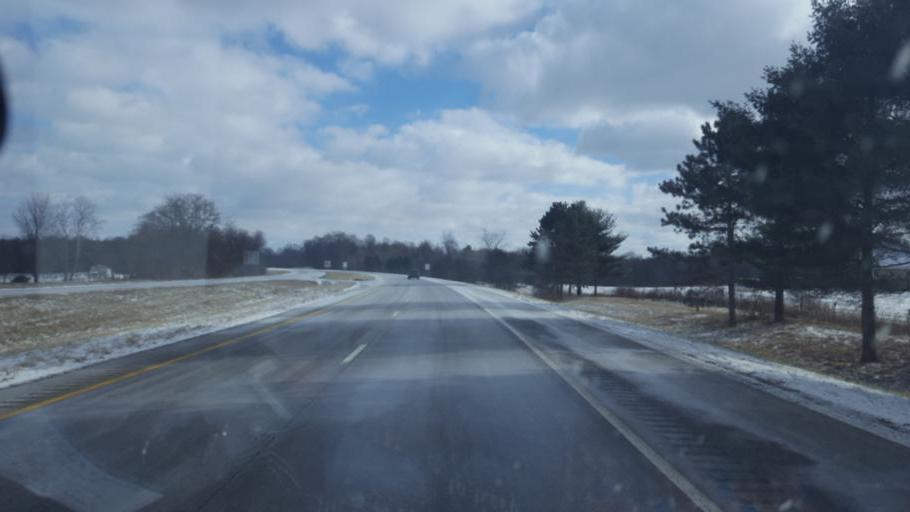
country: US
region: Ohio
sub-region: Muskingum County
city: Frazeysburg
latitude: 40.0797
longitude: -82.2208
